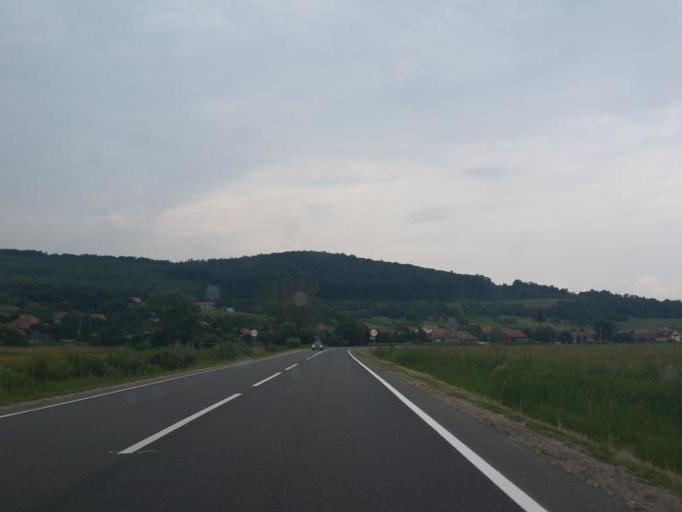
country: RO
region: Cluj
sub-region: Comuna Sanpaul
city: Sanpaul
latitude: 46.8934
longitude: 23.4103
